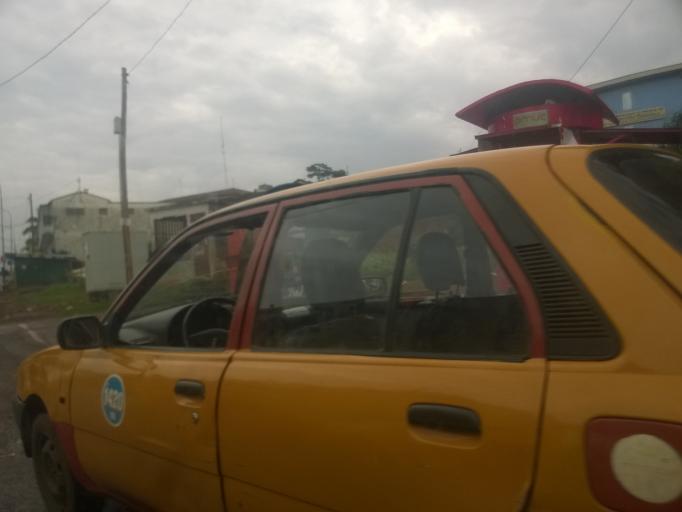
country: CM
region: Centre
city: Yaounde
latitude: 3.8689
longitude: 11.5170
